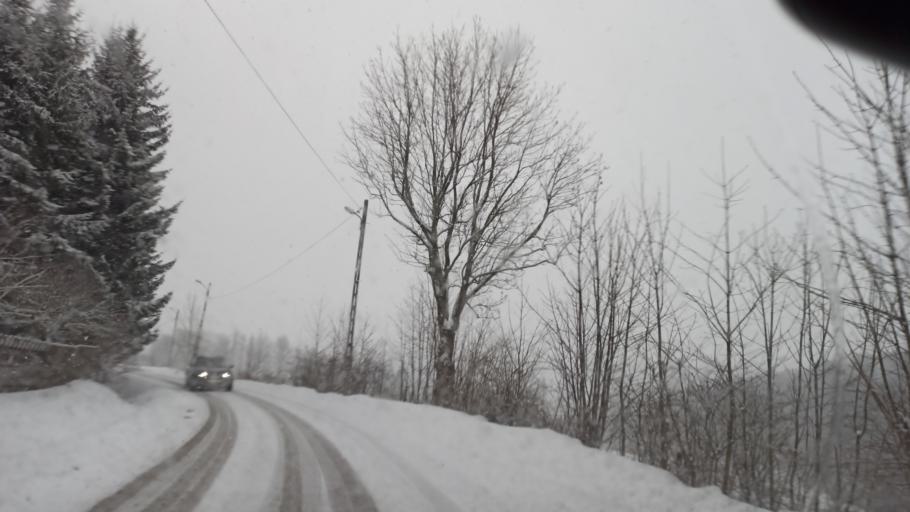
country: PL
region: Lower Silesian Voivodeship
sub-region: Powiat klodzki
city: Ludwikowice Klodzkie
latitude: 50.6510
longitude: 16.4729
